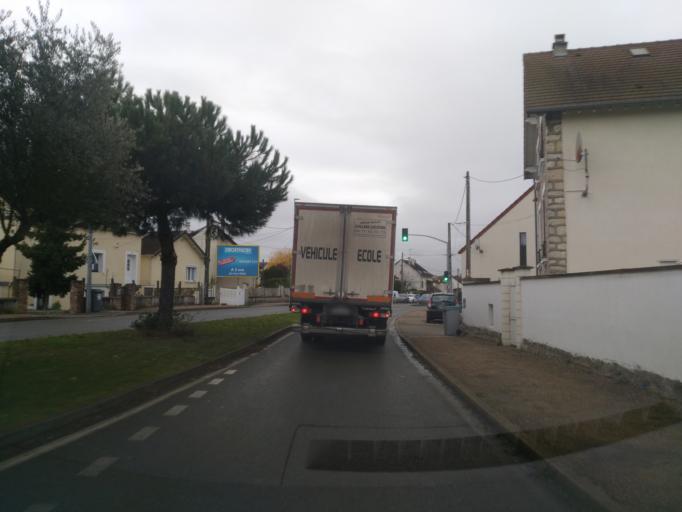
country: FR
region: Ile-de-France
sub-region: Departement des Yvelines
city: Villepreux
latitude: 48.8195
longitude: 2.0020
